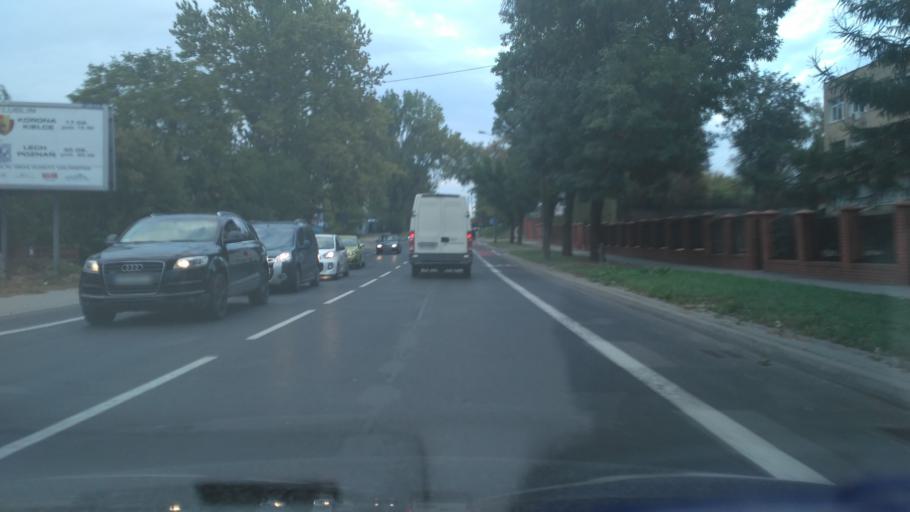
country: PL
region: Lublin Voivodeship
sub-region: Powiat lubelski
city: Lublin
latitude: 51.2531
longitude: 22.6008
